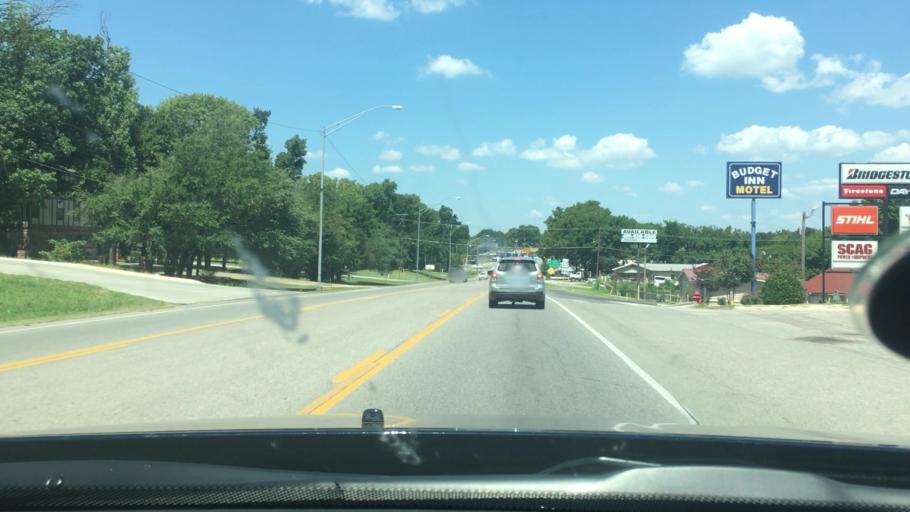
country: US
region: Oklahoma
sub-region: Marshall County
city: Madill
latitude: 34.0813
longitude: -96.7657
